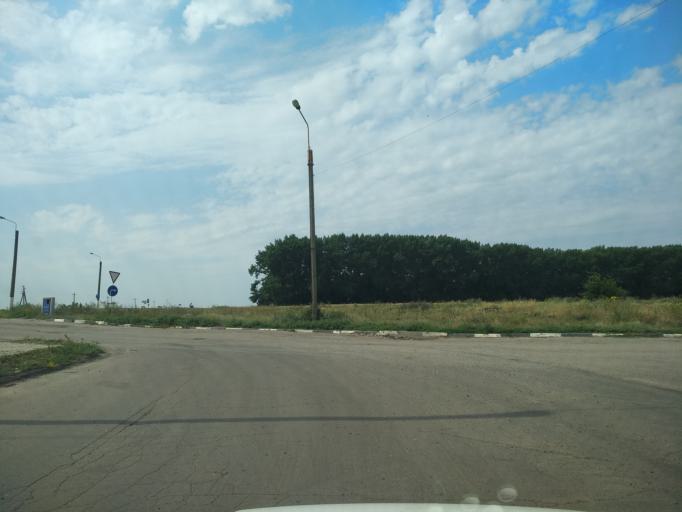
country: RU
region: Lipetsk
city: Dobrinka
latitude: 51.9018
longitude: 40.4547
